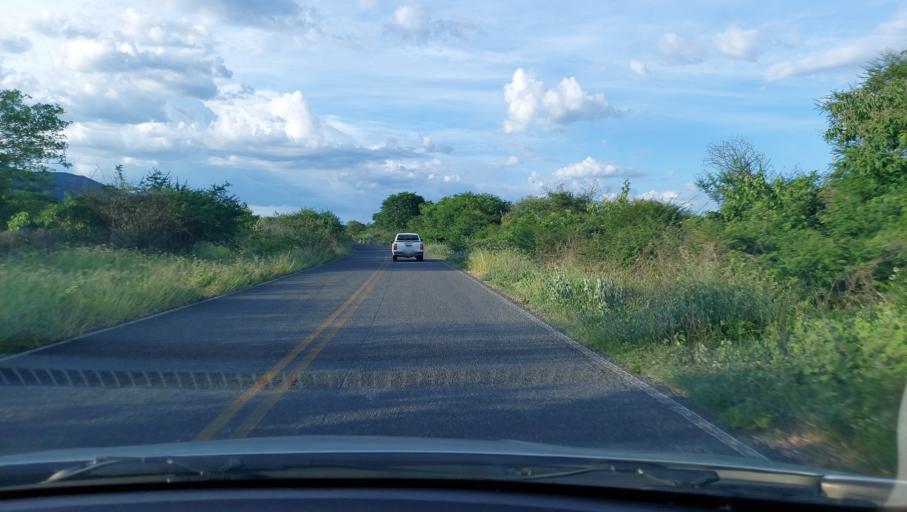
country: BR
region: Bahia
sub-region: Oliveira Dos Brejinhos
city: Beira Rio
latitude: -12.1929
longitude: -42.5373
